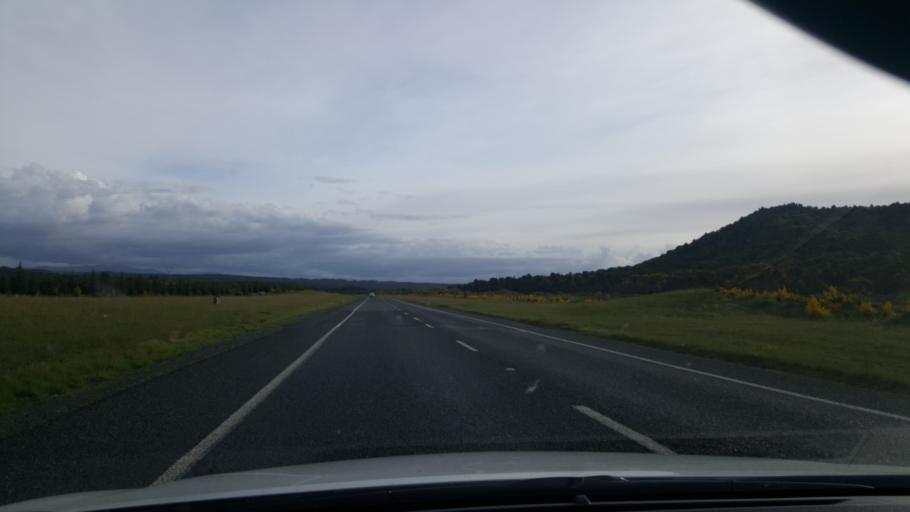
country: NZ
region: Waikato
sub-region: Taupo District
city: Taupo
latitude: -38.8445
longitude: 176.0589
